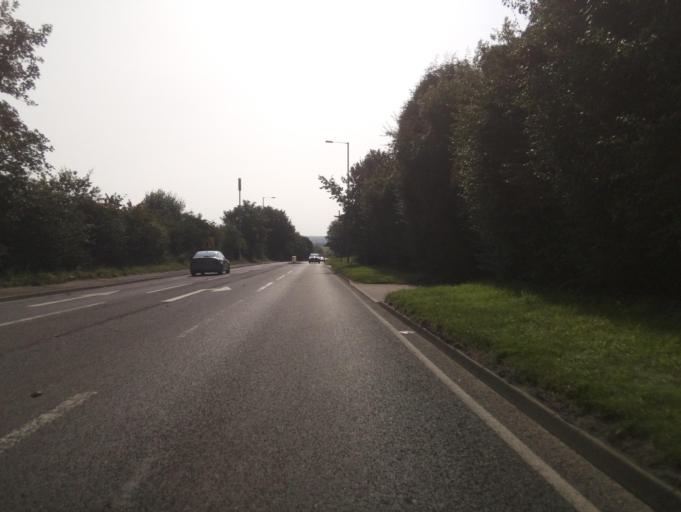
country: GB
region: England
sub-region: Walsall
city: Aldridge
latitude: 52.6296
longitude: -1.9076
